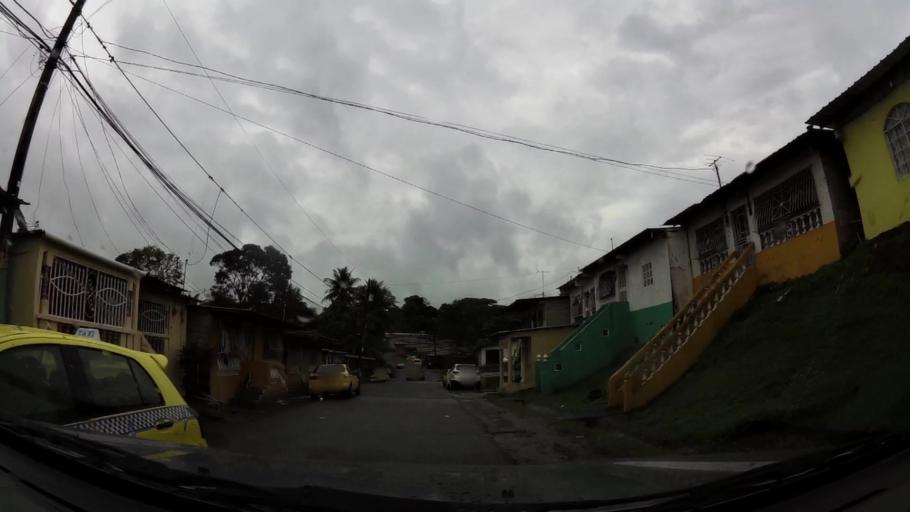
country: PA
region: Colon
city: Las Margaritas
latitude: 9.3324
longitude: -79.8696
